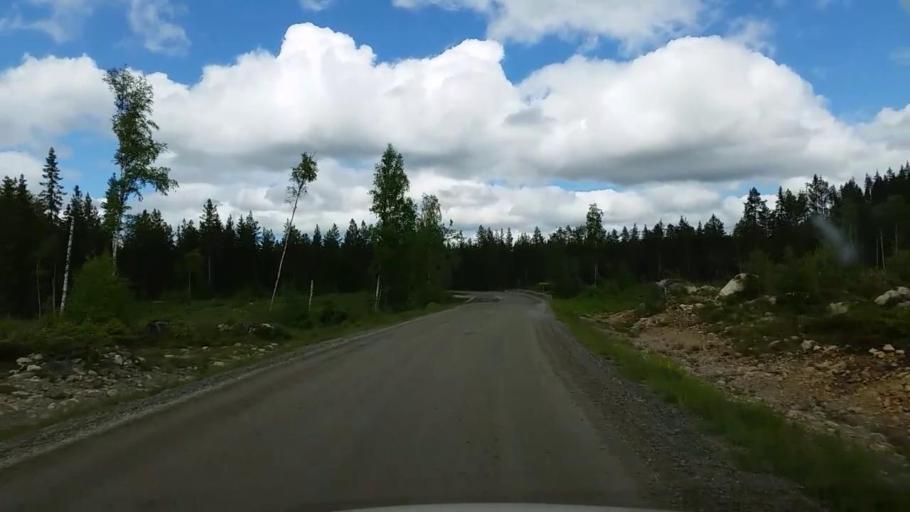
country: SE
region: Gaevleborg
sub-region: Bollnas Kommun
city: Vittsjo
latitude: 61.1528
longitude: 16.1598
